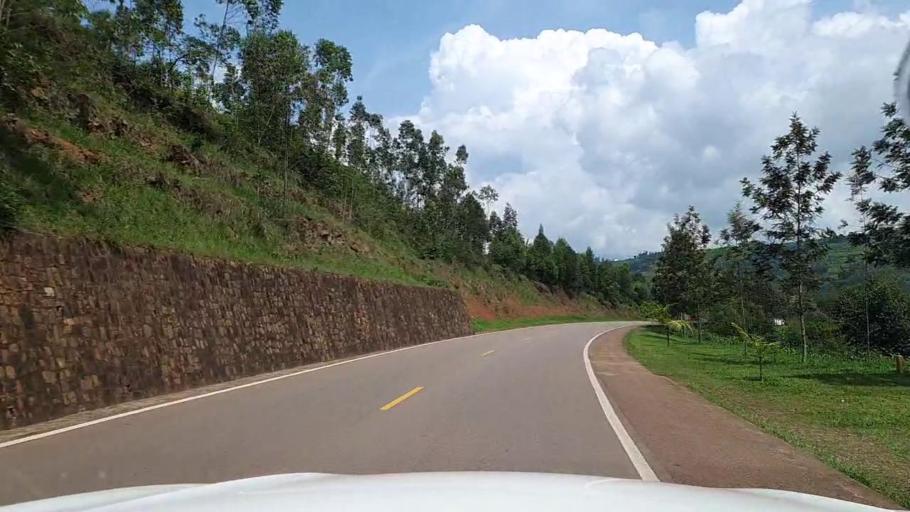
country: RW
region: Kigali
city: Kigali
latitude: -1.8284
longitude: 30.0787
